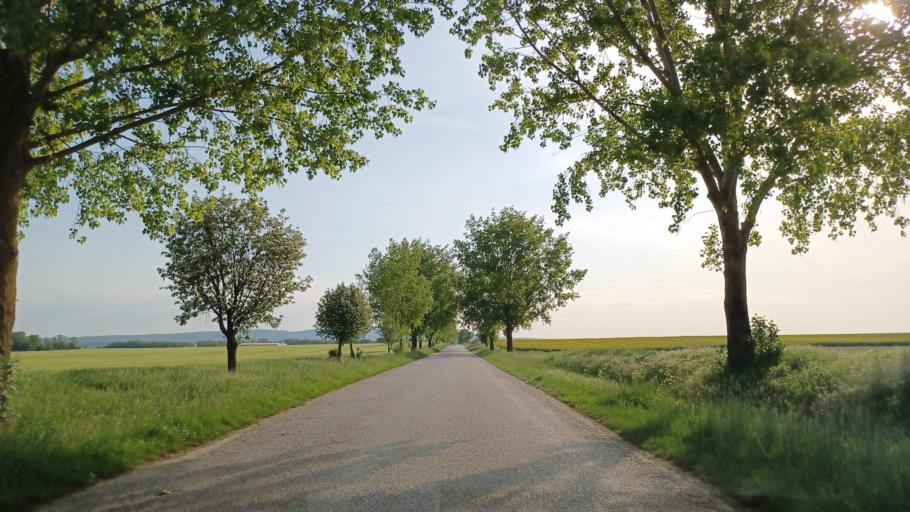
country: HU
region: Baranya
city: Villany
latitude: 45.9533
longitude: 18.3793
